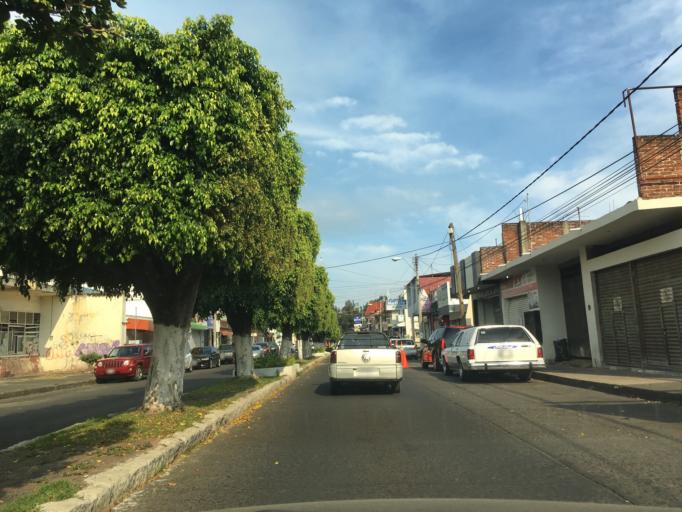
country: MX
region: Michoacan
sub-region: Uruapan
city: Uruapan
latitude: 19.4157
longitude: -102.0544
